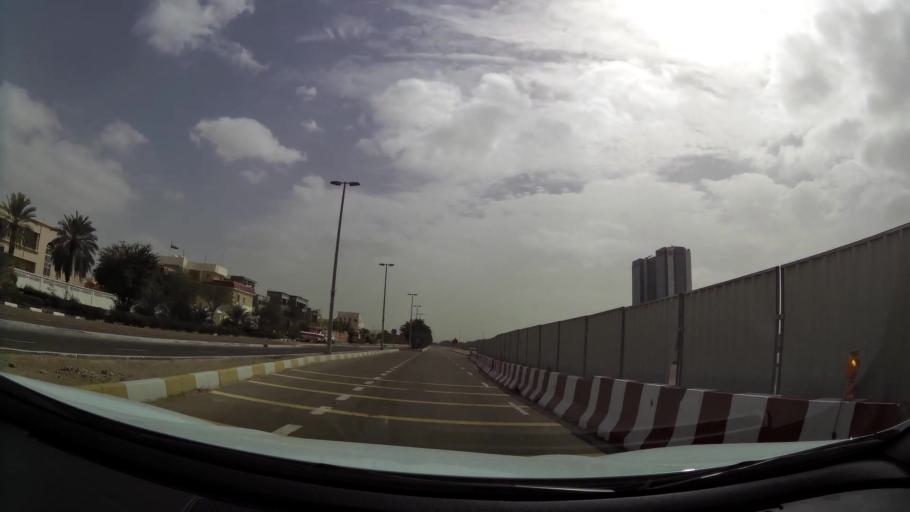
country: AE
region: Abu Dhabi
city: Abu Dhabi
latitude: 24.3985
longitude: 54.5152
